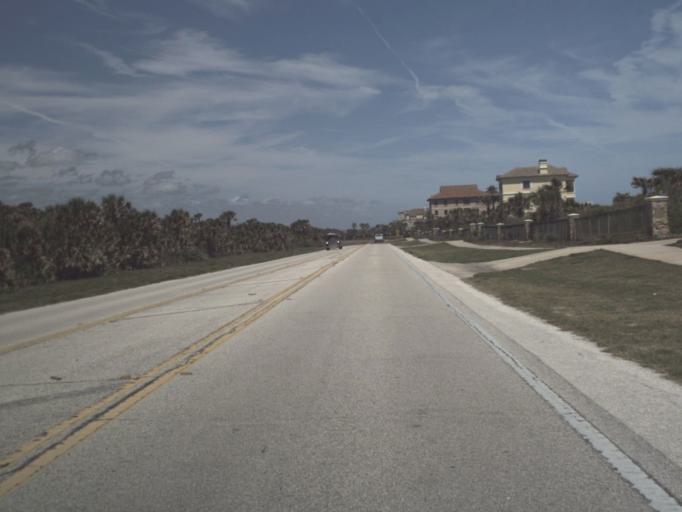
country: US
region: Florida
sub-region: Flagler County
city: Palm Coast
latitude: 29.5571
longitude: -81.1655
